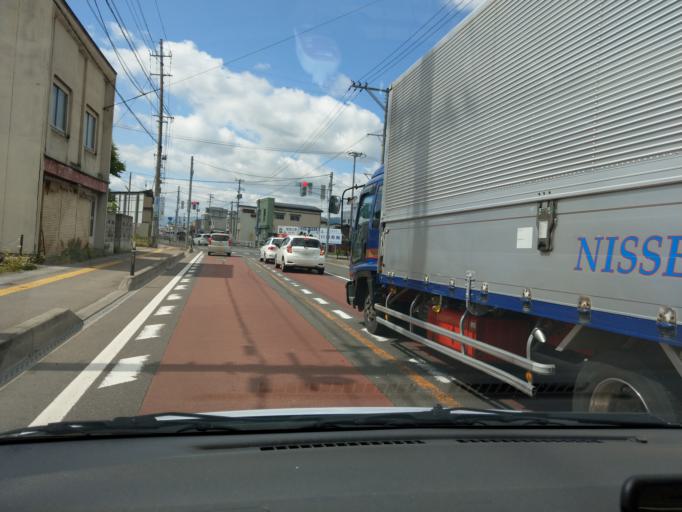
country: JP
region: Akita
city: Yuzawa
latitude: 39.1699
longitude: 140.4906
